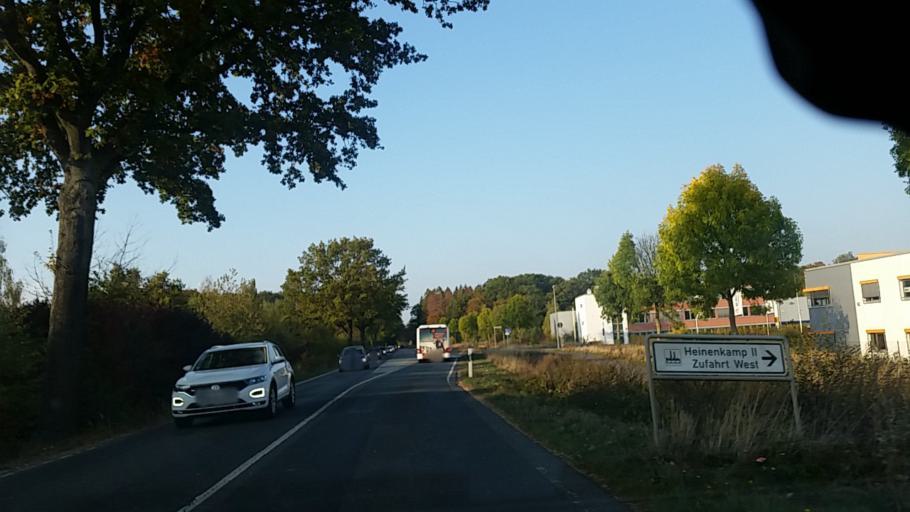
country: DE
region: Lower Saxony
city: Wolfsburg
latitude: 52.3720
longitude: 10.7450
